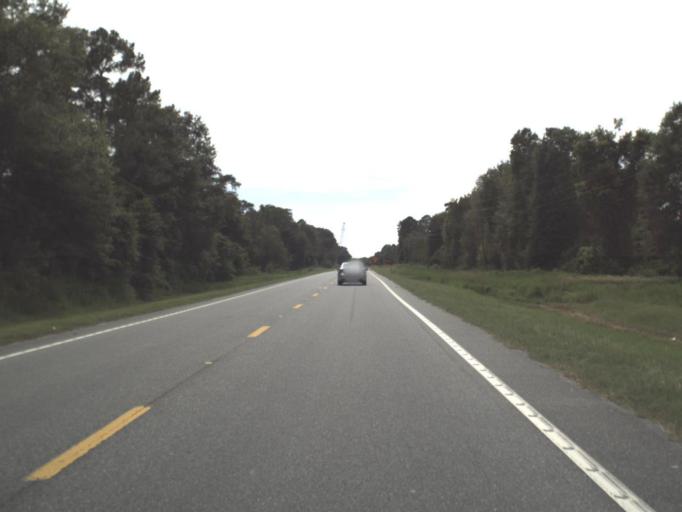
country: US
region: Florida
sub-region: Taylor County
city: Perry
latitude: 30.0994
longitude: -83.4624
